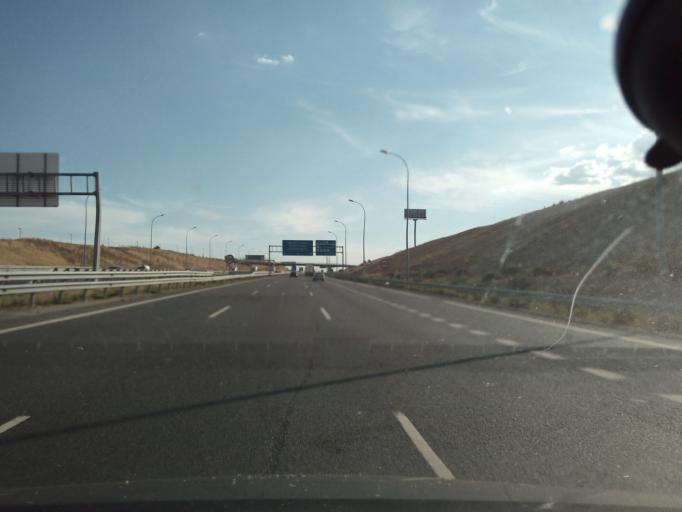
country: ES
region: Madrid
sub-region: Provincia de Madrid
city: Villa de Vallecas
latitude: 40.3515
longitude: -3.5771
